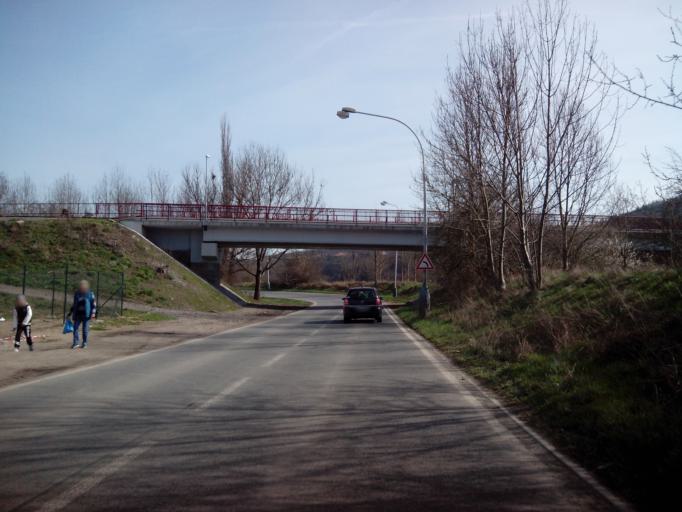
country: CZ
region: Central Bohemia
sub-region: Okres Beroun
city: Beroun
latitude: 49.9613
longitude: 14.0870
